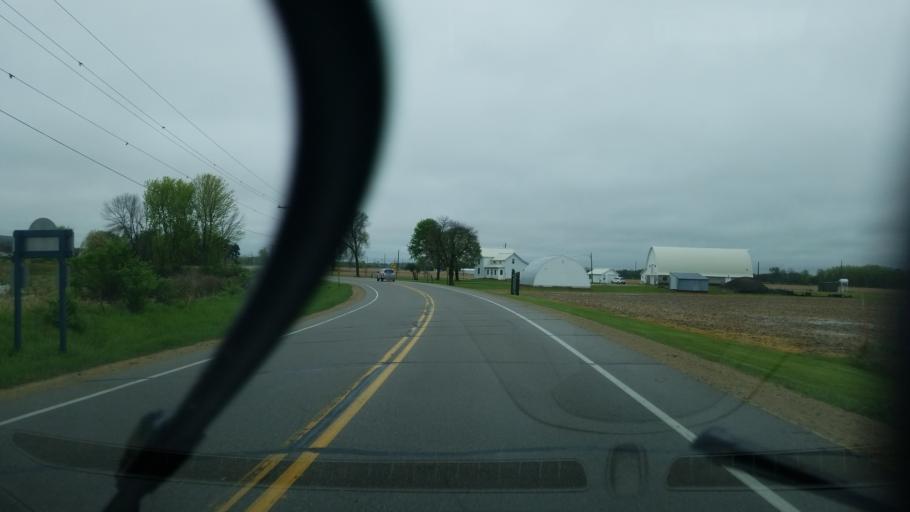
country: US
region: Wisconsin
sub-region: Dane County
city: Fitchburg
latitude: 42.9434
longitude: -89.4387
